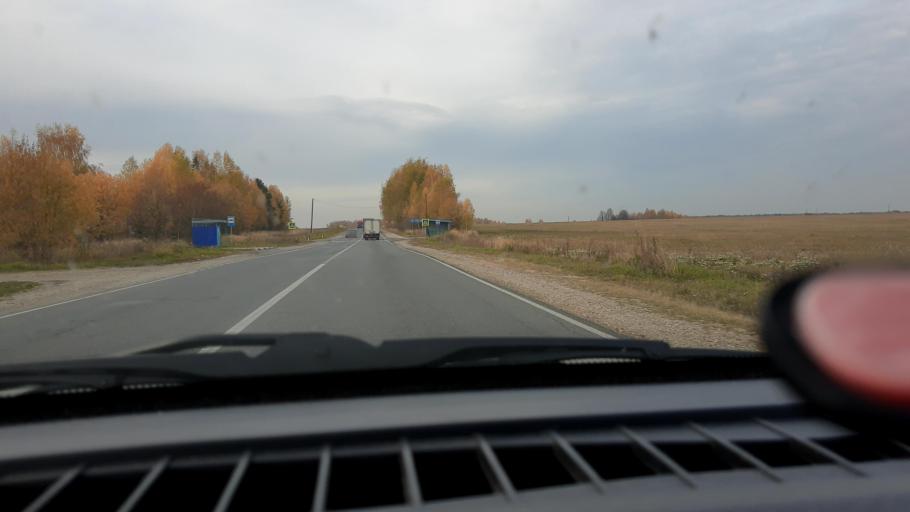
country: RU
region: Nizjnij Novgorod
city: Gorodets
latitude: 56.6240
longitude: 43.5491
